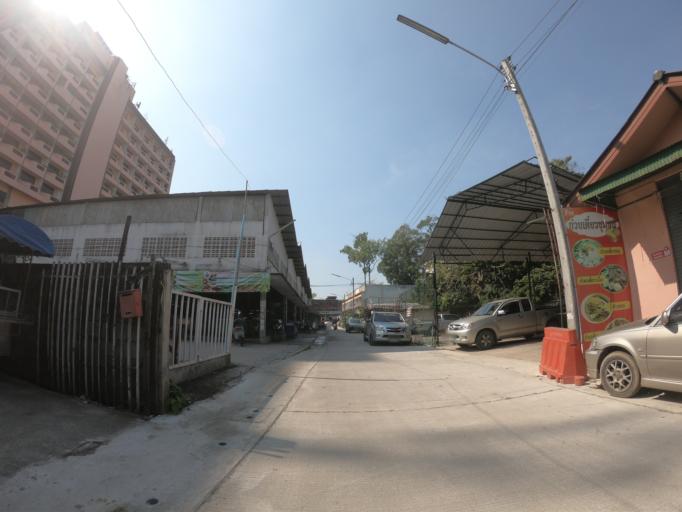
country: TH
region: Chiang Mai
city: Chiang Mai
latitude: 18.7644
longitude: 99.0068
